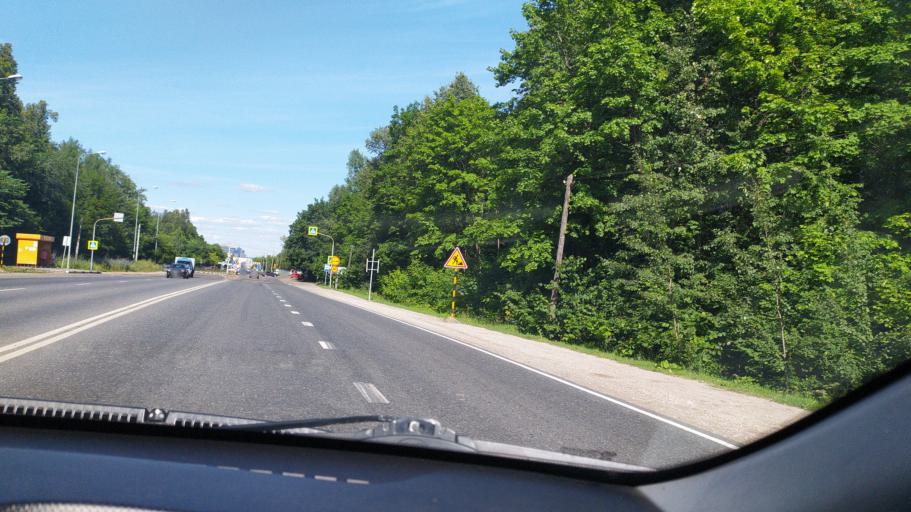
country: RU
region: Chuvashia
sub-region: Cheboksarskiy Rayon
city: Cheboksary
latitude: 56.0955
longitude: 47.2566
